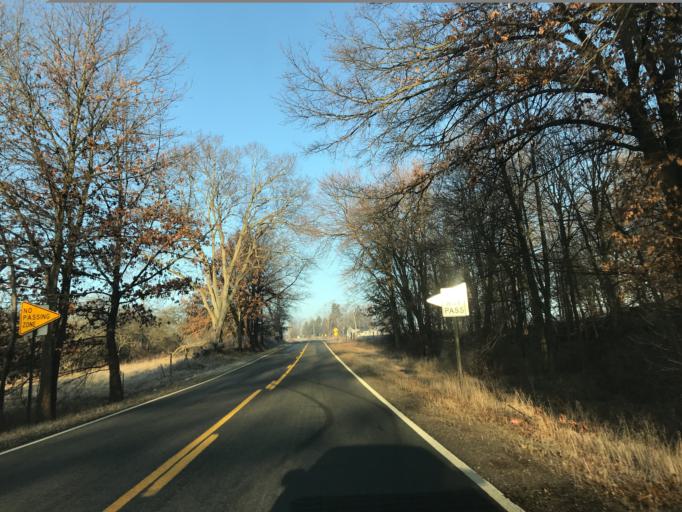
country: US
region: Michigan
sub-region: Eaton County
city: Eaton Rapids
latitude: 42.4491
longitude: -84.5702
